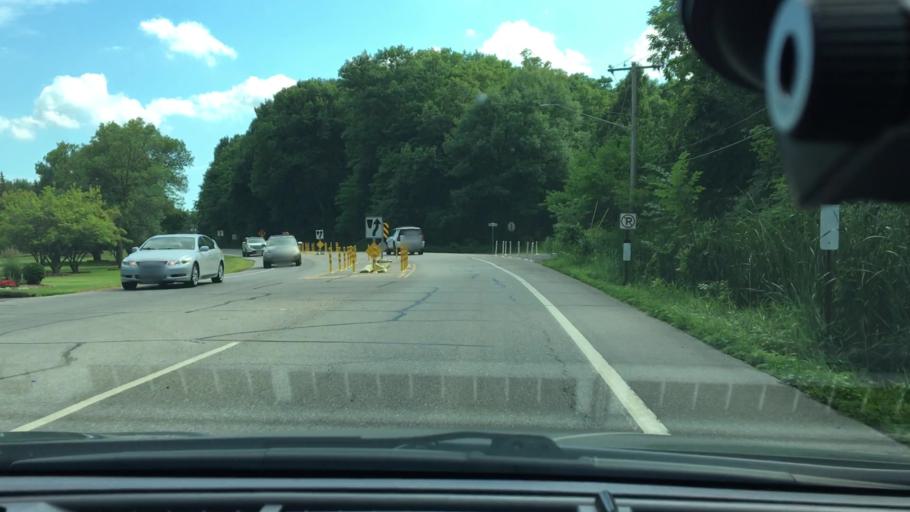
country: US
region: Minnesota
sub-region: Hennepin County
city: Tonka Bay
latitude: 44.9418
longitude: -93.5813
